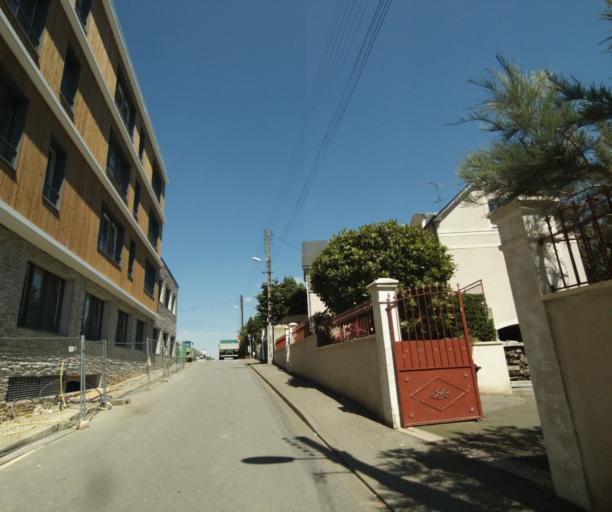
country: FR
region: Pays de la Loire
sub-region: Departement de la Mayenne
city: Laval
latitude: 48.0700
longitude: -0.7563
